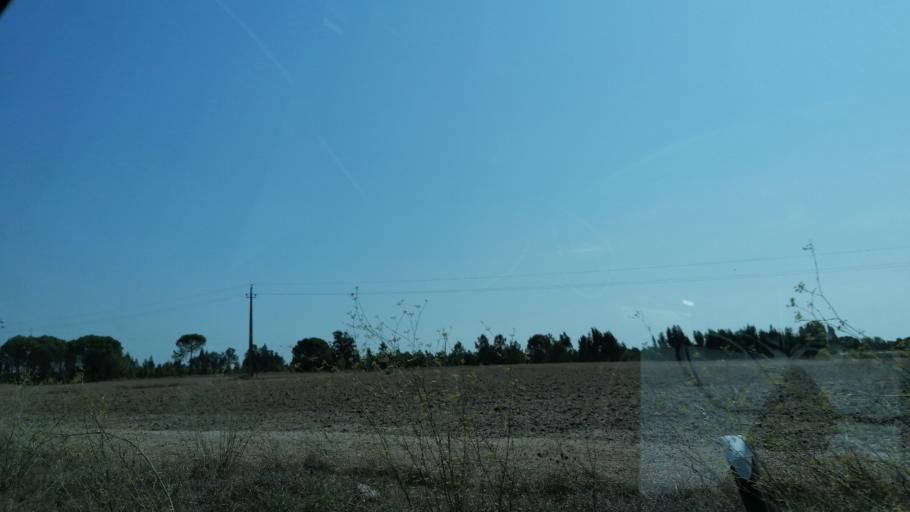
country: PT
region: Santarem
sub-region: Benavente
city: Poceirao
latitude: 38.7252
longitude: -8.6425
